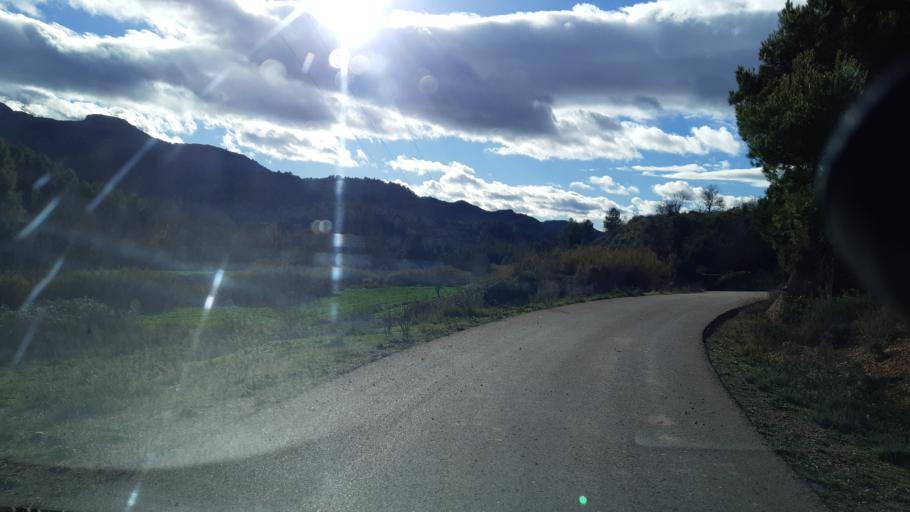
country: ES
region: Aragon
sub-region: Provincia de Teruel
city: Valderrobres
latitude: 40.8464
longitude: 0.2078
